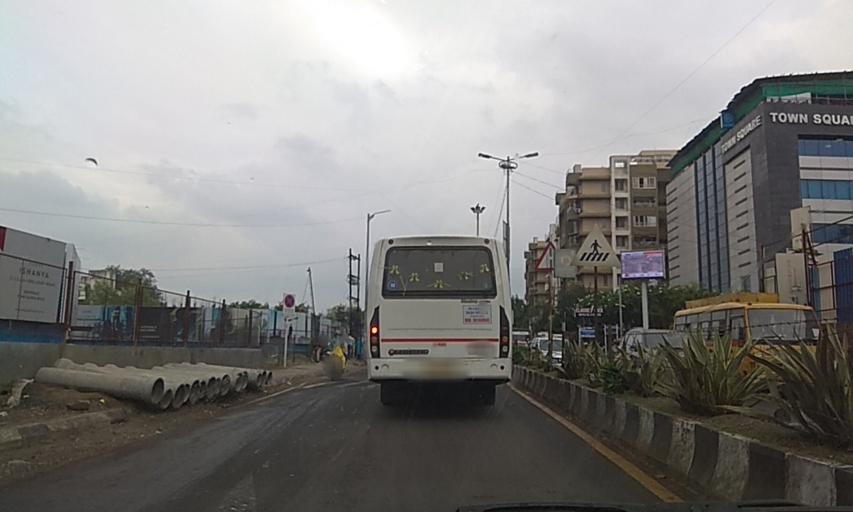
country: IN
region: Maharashtra
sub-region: Pune Division
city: Lohogaon
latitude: 18.5680
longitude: 73.9067
